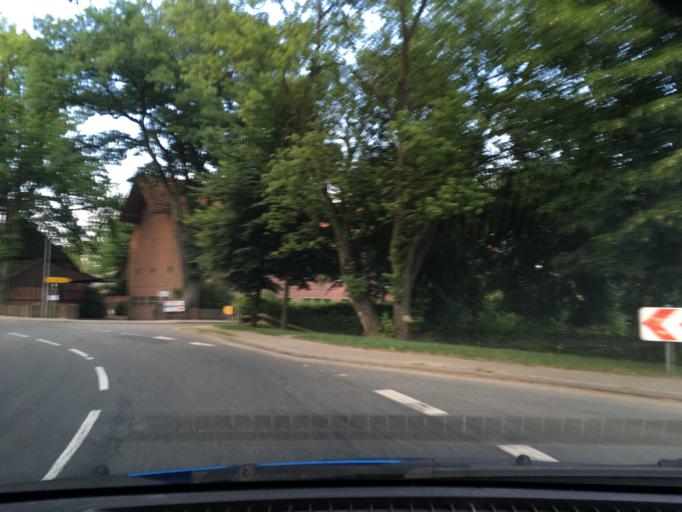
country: DE
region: Lower Saxony
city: Steinhorst
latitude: 52.6885
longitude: 10.4027
